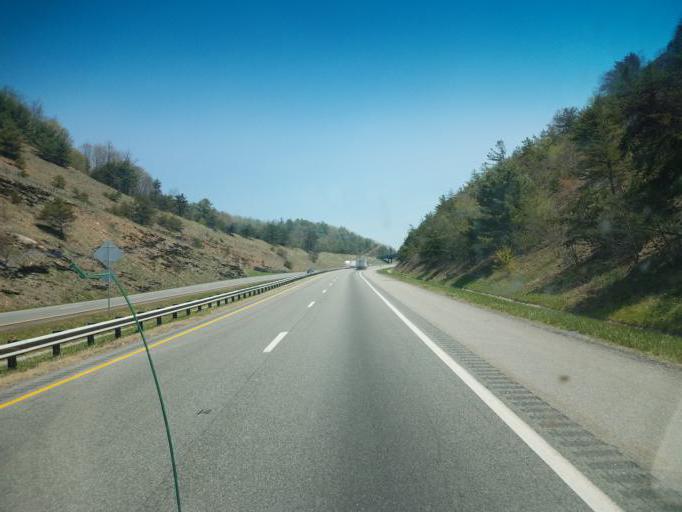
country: US
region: Virginia
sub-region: Bland County
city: Bland
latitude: 37.1393
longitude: -81.1306
